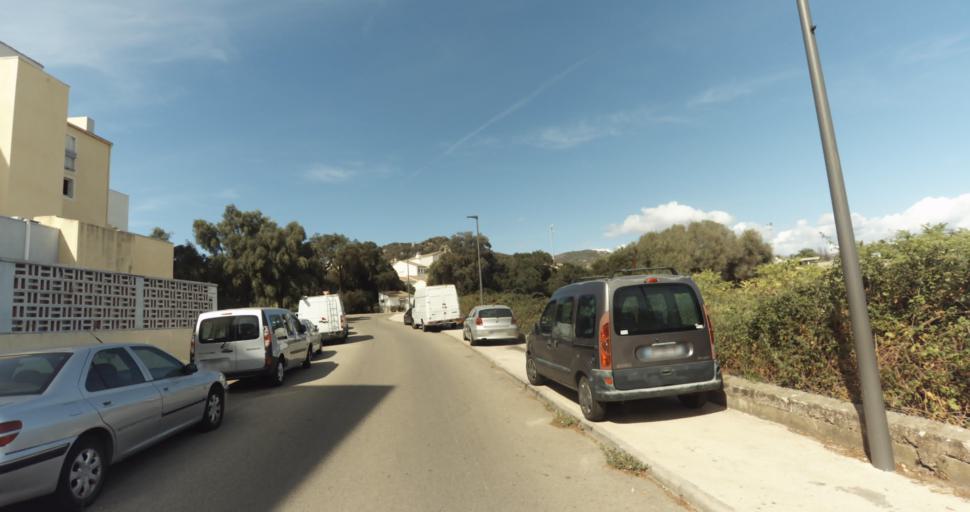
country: FR
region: Corsica
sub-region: Departement de la Corse-du-Sud
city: Ajaccio
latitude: 41.9478
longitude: 8.7551
